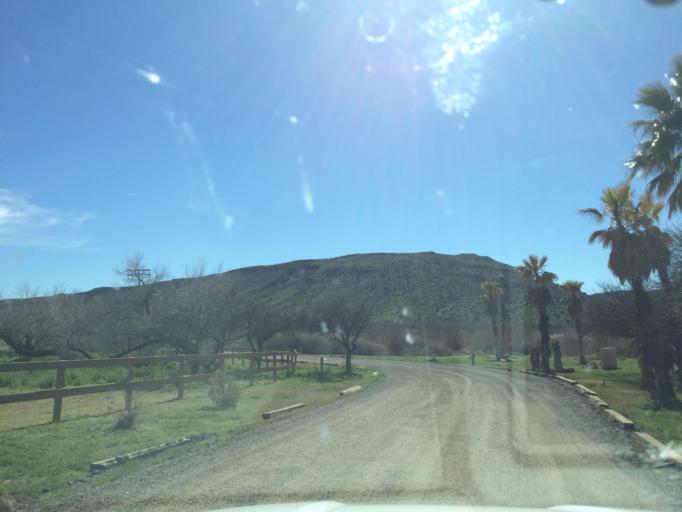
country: MX
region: Baja California
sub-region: Tecate
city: Cereso del Hongo
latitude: 32.6522
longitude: -116.1867
